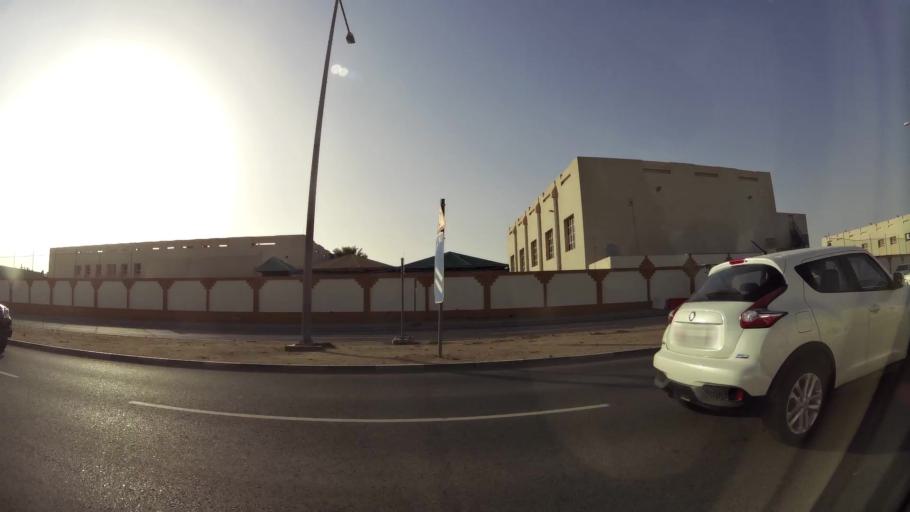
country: QA
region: Baladiyat ar Rayyan
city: Ar Rayyan
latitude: 25.3395
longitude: 51.4498
